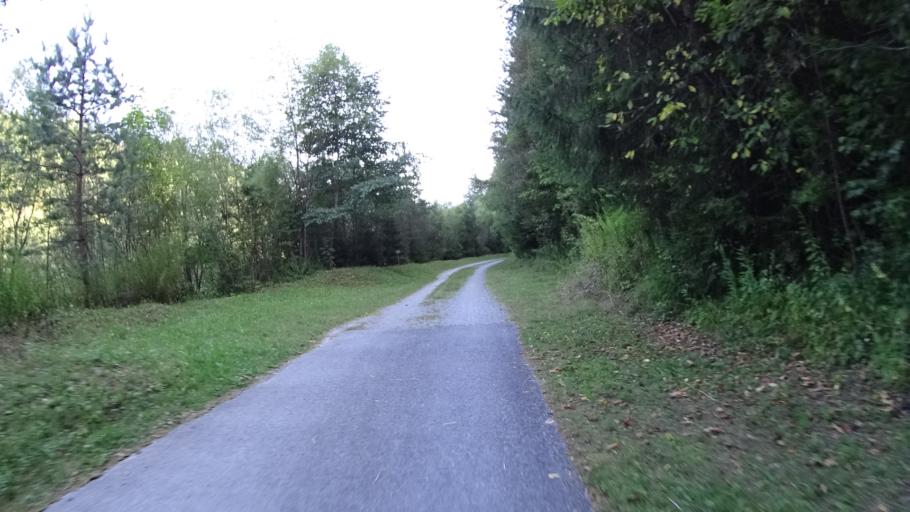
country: AT
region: Carinthia
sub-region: Politischer Bezirk Villach Land
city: Rosegg
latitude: 46.5782
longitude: 14.0194
